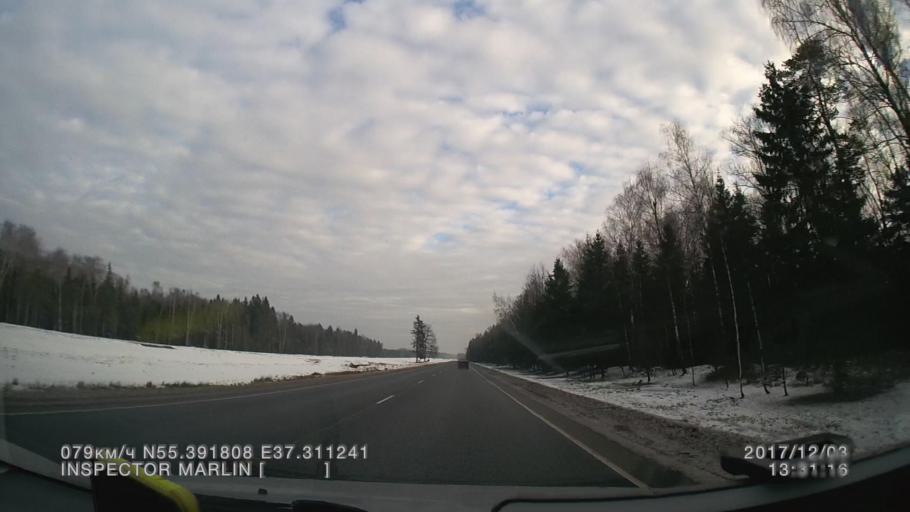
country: RU
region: Moskovskaya
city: Troitsk
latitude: 55.3918
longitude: 37.3115
